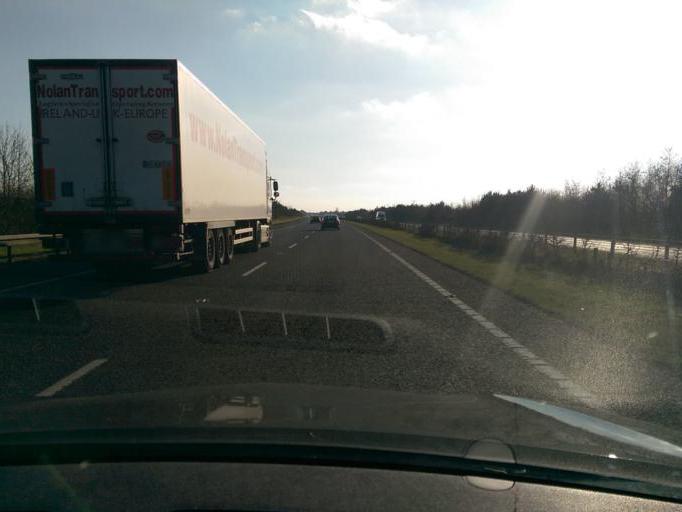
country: IE
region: Leinster
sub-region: Laois
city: Stradbally
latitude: 53.0771
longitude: -7.2010
